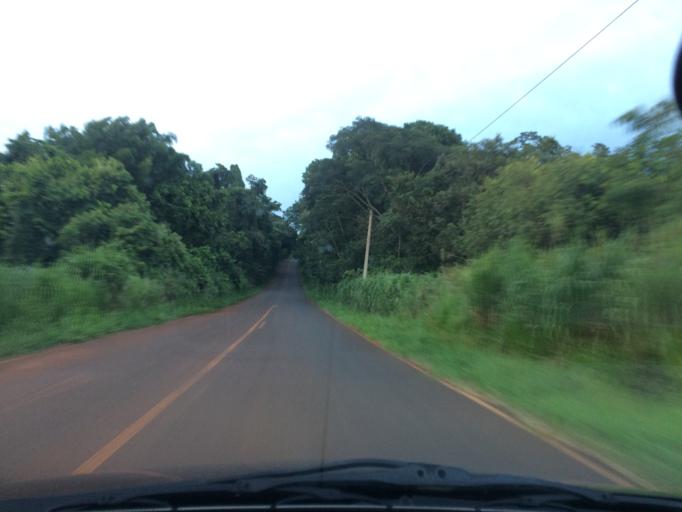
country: BR
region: Sao Paulo
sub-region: Tambau
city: Tambau
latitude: -21.7209
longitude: -47.1905
